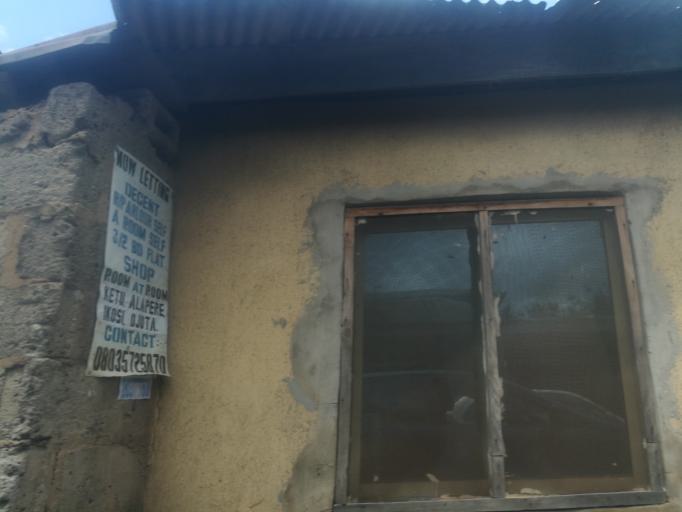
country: NG
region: Lagos
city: Ojota
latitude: 6.6000
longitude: 3.3902
